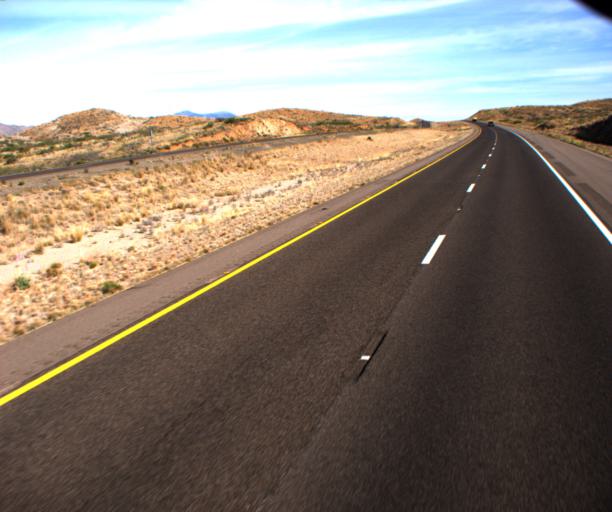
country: US
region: Arizona
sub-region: Cochise County
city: Willcox
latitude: 32.4513
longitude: -109.6638
